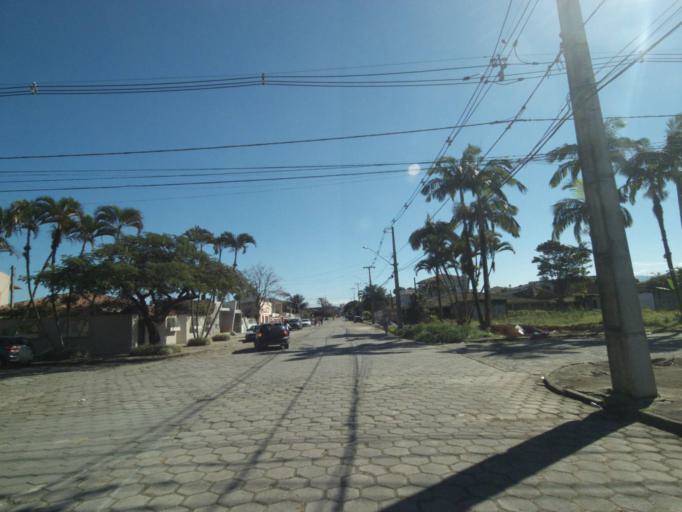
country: BR
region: Parana
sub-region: Paranagua
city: Paranagua
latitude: -25.5126
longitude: -48.5042
